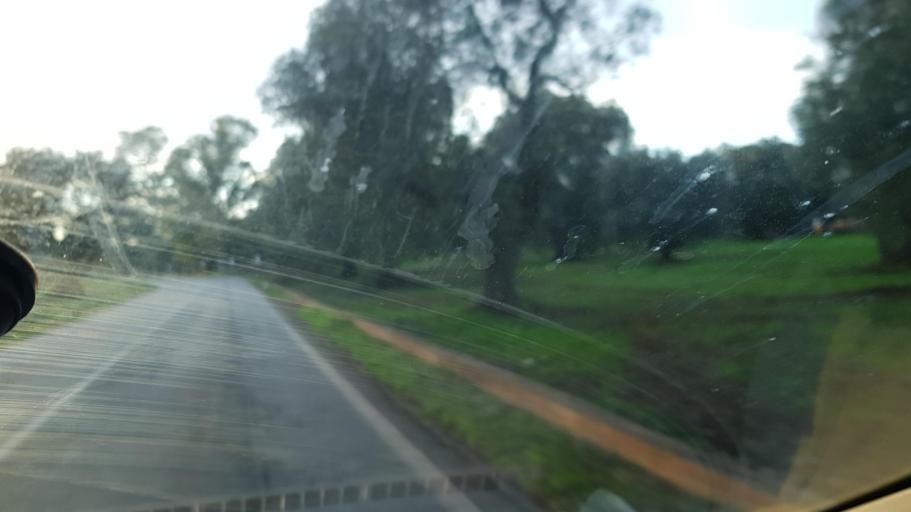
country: IT
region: Apulia
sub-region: Provincia di Brindisi
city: San Michele Salentino
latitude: 40.6426
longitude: 17.5949
